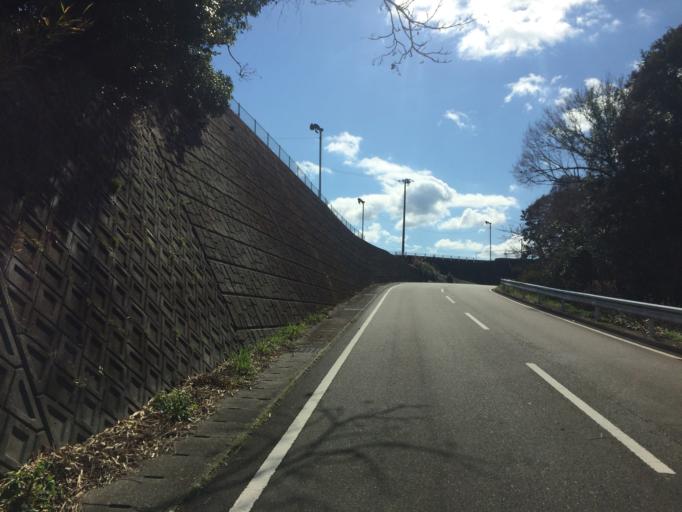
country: JP
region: Shizuoka
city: Shimada
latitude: 34.7572
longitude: 138.1750
